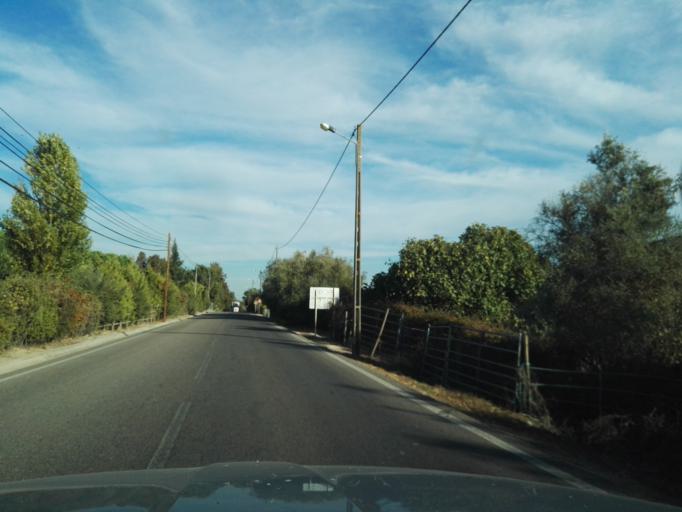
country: PT
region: Santarem
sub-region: Benavente
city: Poceirao
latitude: 38.8579
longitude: -8.7368
